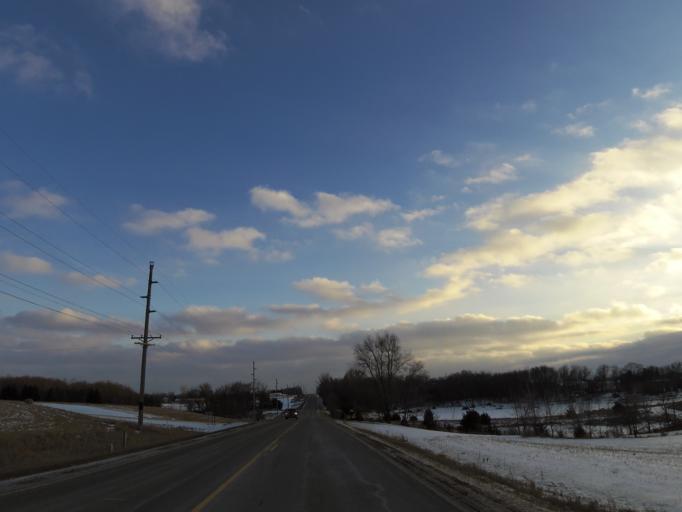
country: US
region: Minnesota
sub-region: Scott County
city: Prior Lake
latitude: 44.6550
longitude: -93.4400
